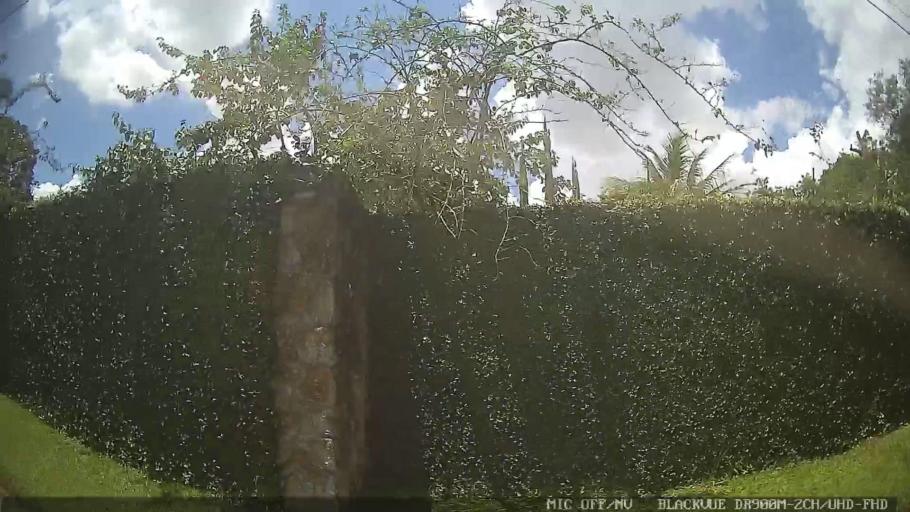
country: BR
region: Sao Paulo
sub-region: Atibaia
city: Atibaia
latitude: -23.1202
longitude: -46.5969
